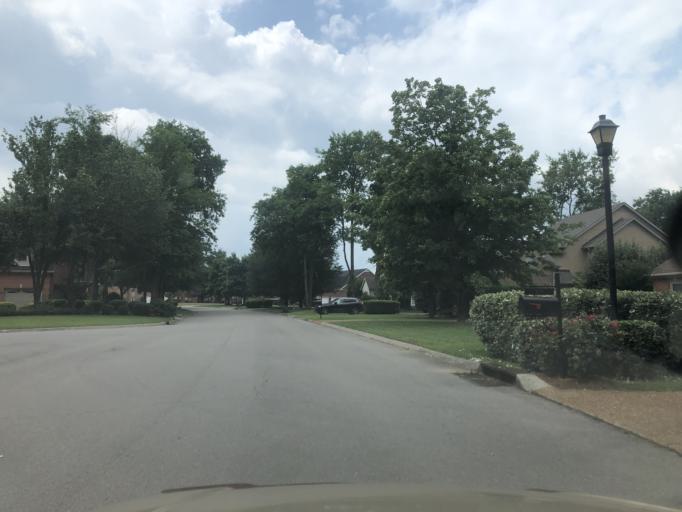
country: US
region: Tennessee
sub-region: Davidson County
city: Lakewood
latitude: 36.2342
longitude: -86.6086
